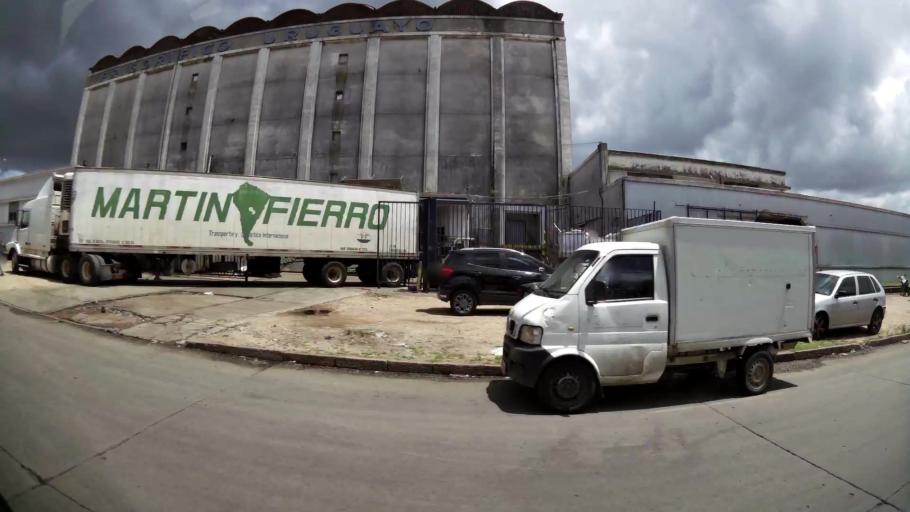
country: UY
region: Montevideo
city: Montevideo
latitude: -34.8706
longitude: -56.1523
